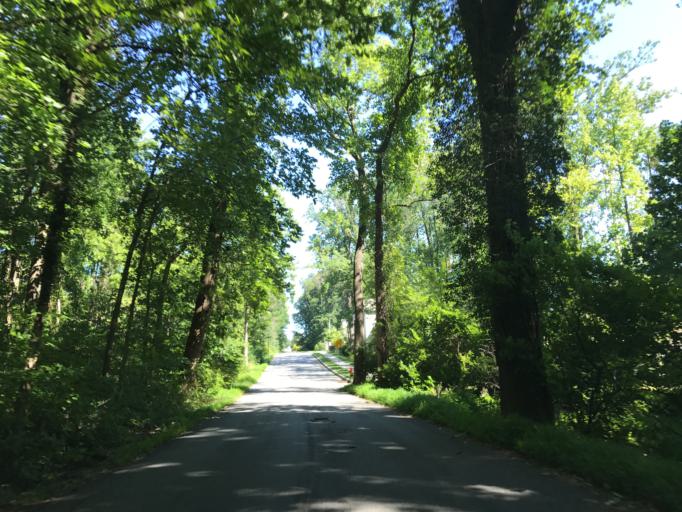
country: US
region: Maryland
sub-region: Howard County
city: Ilchester
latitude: 39.2568
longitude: -76.7572
